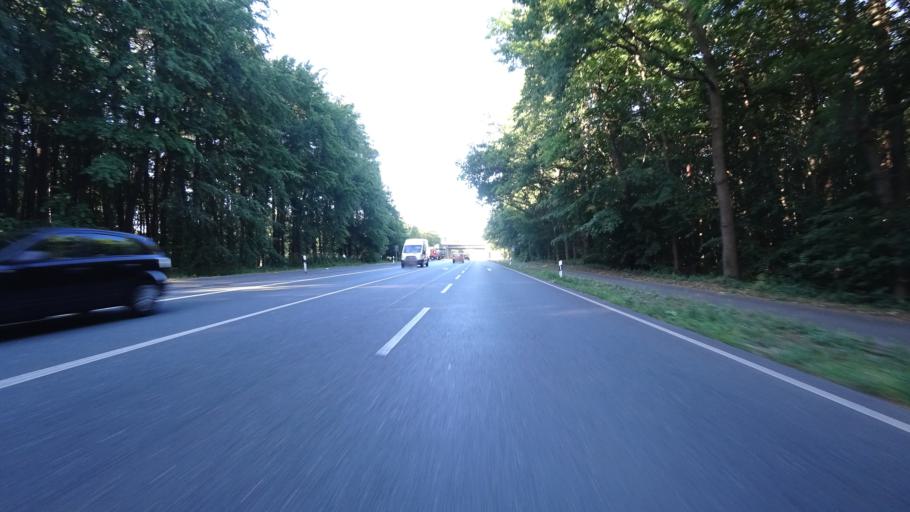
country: DE
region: North Rhine-Westphalia
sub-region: Regierungsbezirk Detmold
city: Rheda-Wiedenbruck
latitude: 51.8538
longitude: 8.3284
